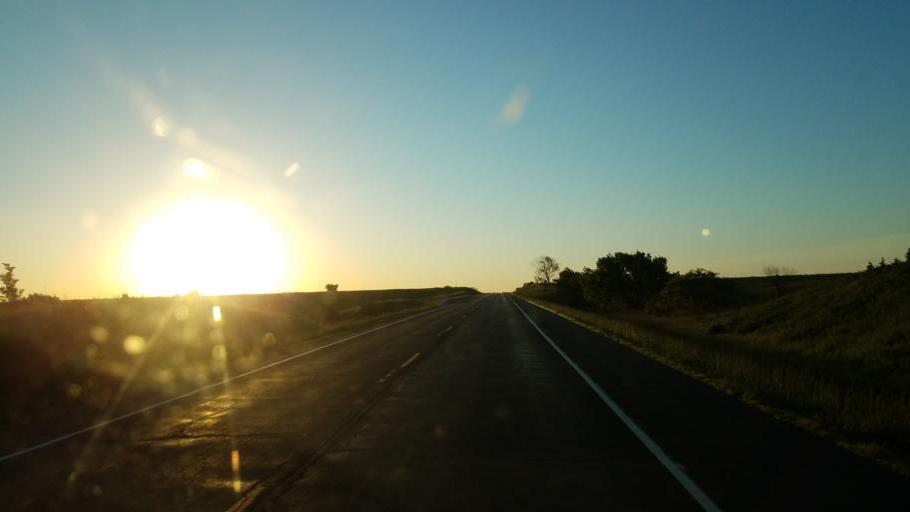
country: US
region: Missouri
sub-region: Schuyler County
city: Lancaster
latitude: 40.4926
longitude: -92.5878
